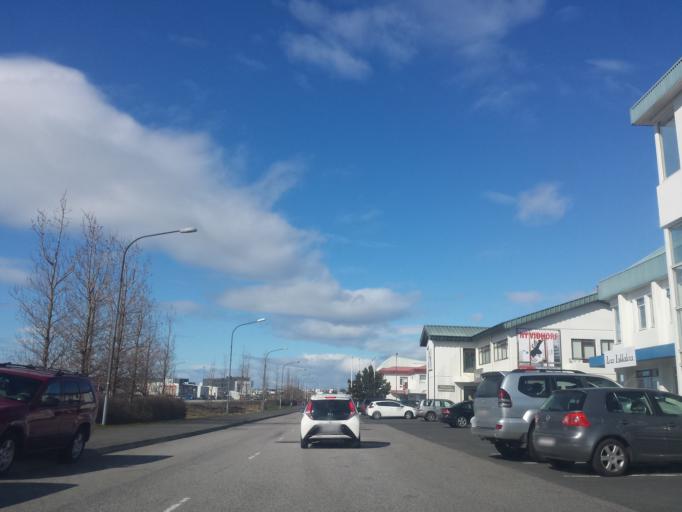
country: IS
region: Capital Region
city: Hafnarfjoerdur
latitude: 64.0780
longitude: -21.9401
